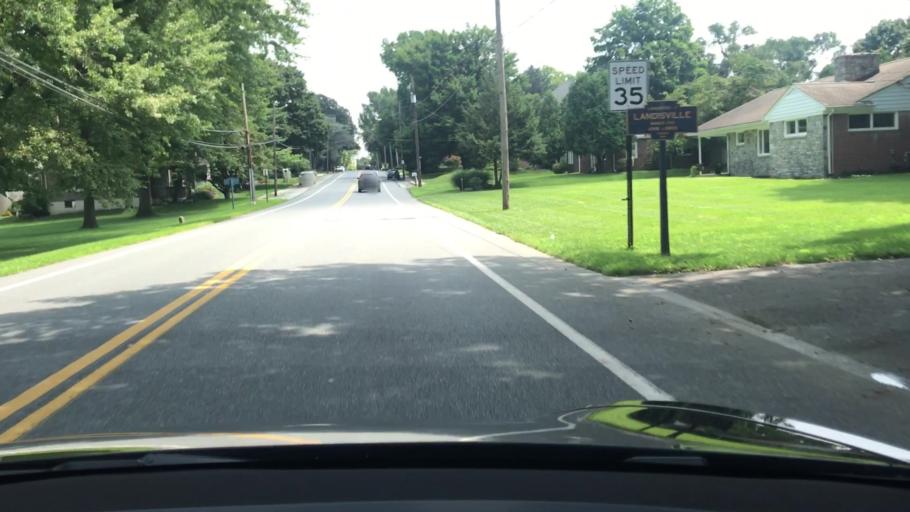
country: US
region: Pennsylvania
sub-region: Lancaster County
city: Salunga
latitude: 40.0997
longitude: -76.4221
